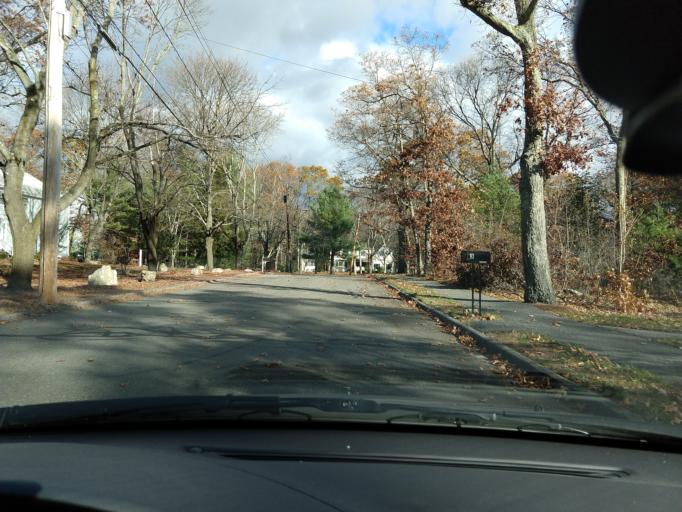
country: US
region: Massachusetts
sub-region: Middlesex County
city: Bedford
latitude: 42.4906
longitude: -71.2459
